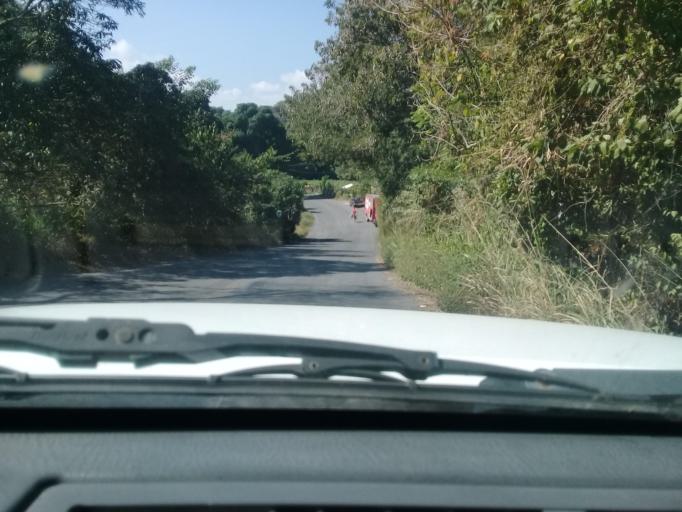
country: MX
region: Veracruz
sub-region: Emiliano Zapata
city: Plan del Rio
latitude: 19.4254
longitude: -96.6101
